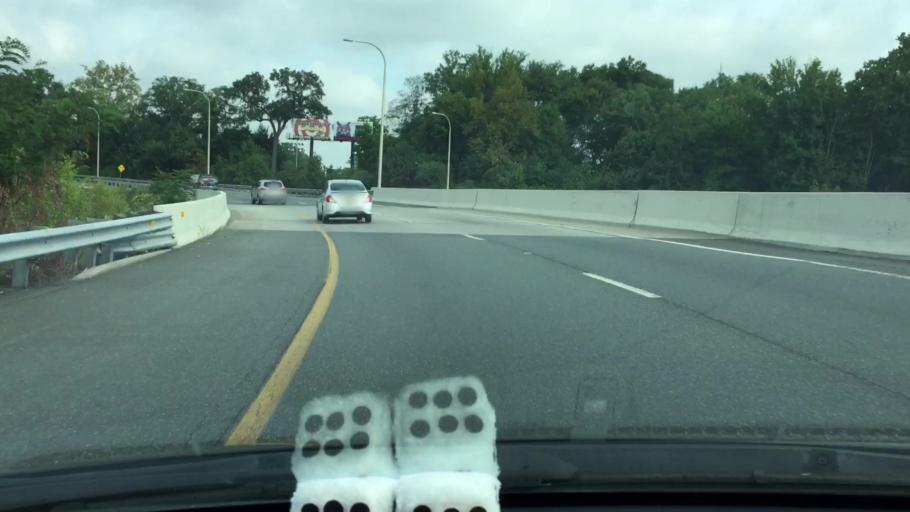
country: US
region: Delaware
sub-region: New Castle County
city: Wilmington
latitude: 39.7682
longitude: -75.5407
